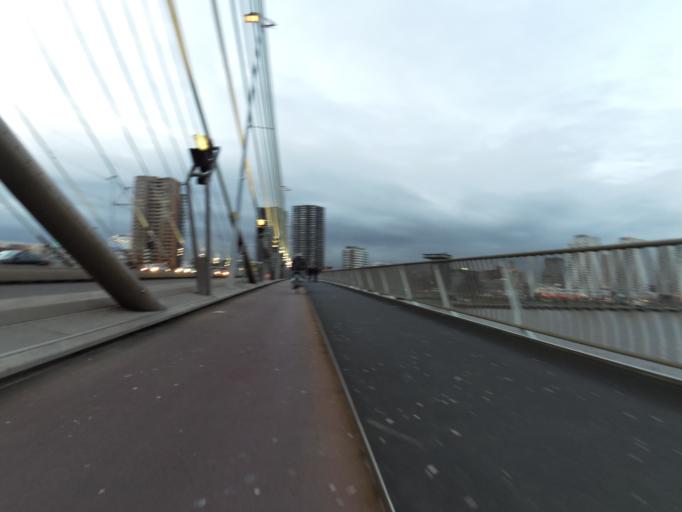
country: NL
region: South Holland
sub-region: Gemeente Rotterdam
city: Rotterdam
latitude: 51.9095
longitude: 4.4862
